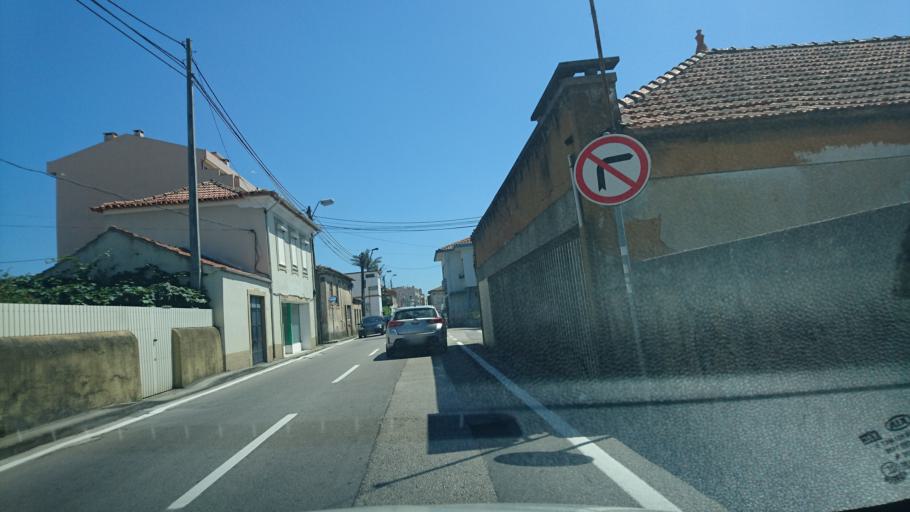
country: PT
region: Aveiro
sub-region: Ovar
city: Esmoriz
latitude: 40.9602
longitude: -8.6276
